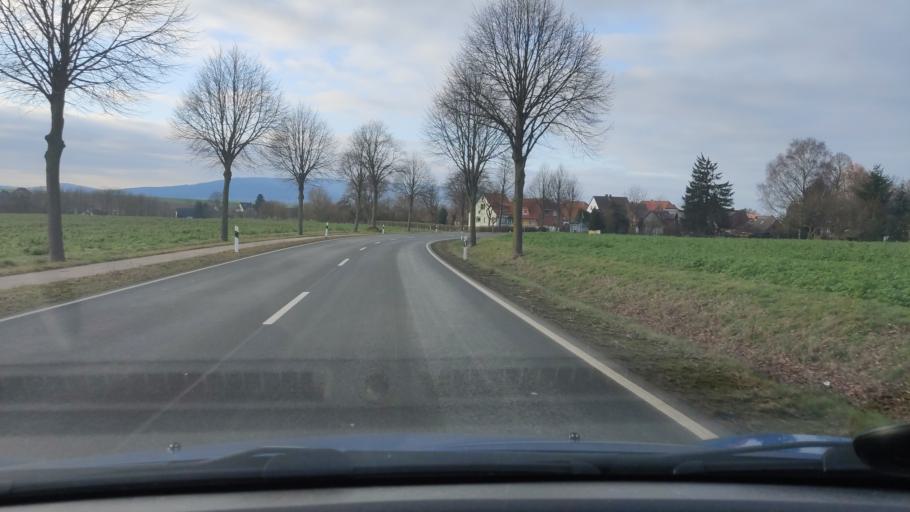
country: DE
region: Lower Saxony
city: Coppenbrugge
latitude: 52.1501
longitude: 9.5024
